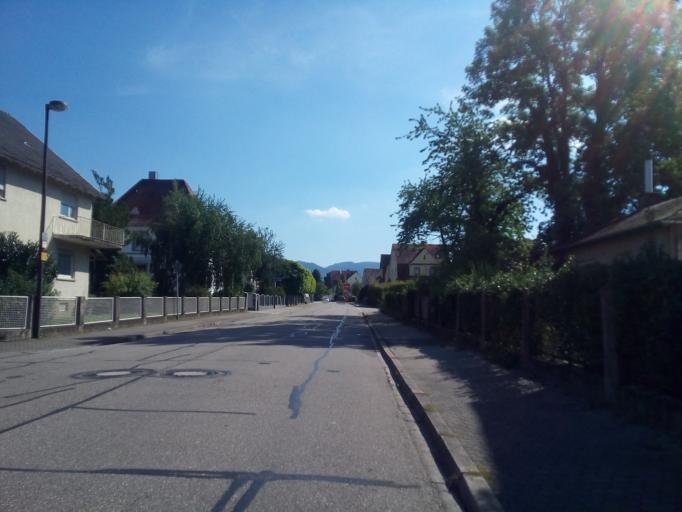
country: DE
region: Baden-Wuerttemberg
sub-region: Freiburg Region
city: Achern
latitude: 48.6218
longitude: 8.0786
